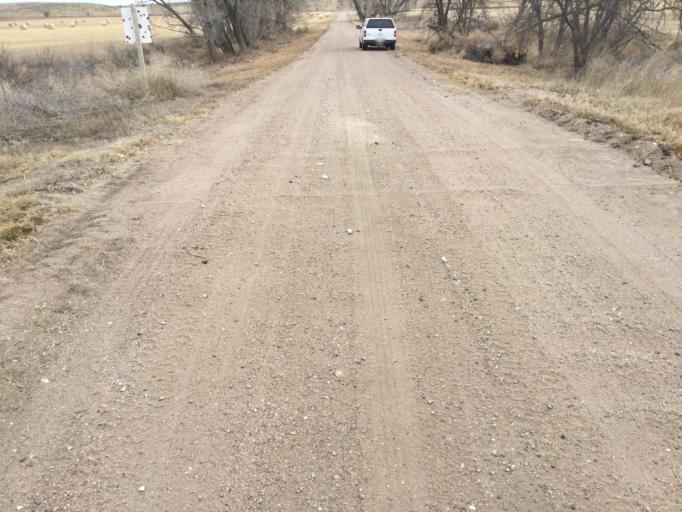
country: US
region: Kansas
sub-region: Rawlins County
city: Atwood
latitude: 39.8234
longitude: -101.0279
